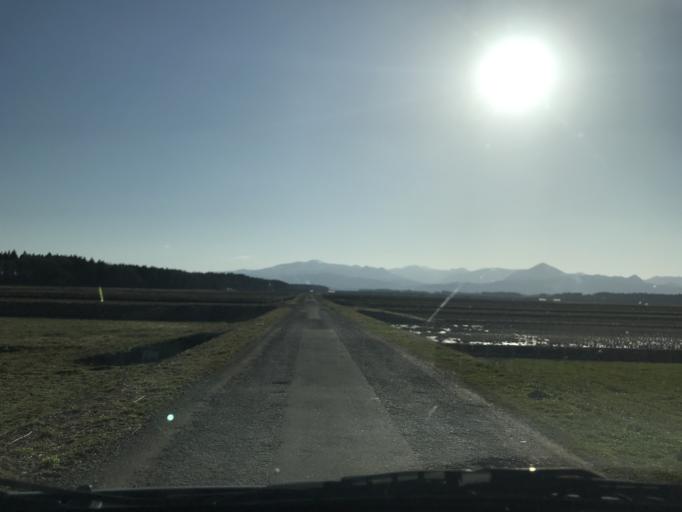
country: JP
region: Iwate
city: Kitakami
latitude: 39.2715
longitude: 141.0641
